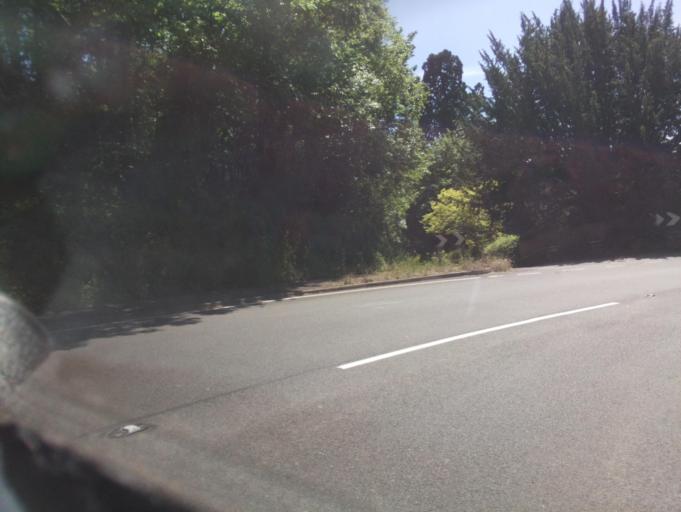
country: GB
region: Wales
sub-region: Monmouthshire
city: Monmouth
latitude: 51.8014
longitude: -2.7138
